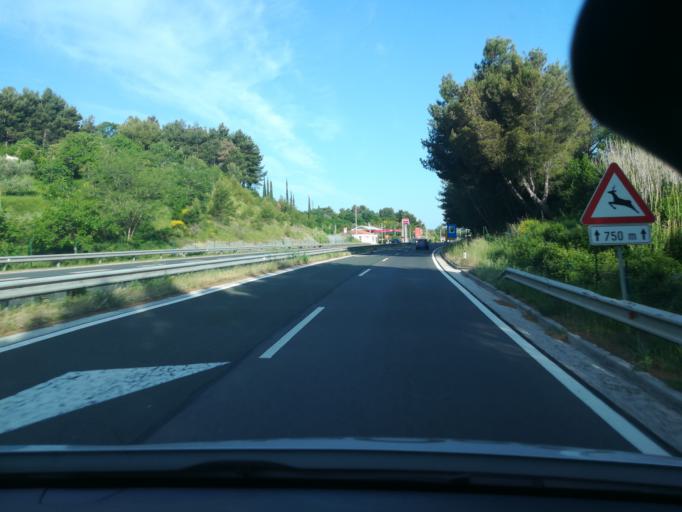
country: SI
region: Izola-Isola
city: Jagodje
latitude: 45.5238
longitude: 13.6535
